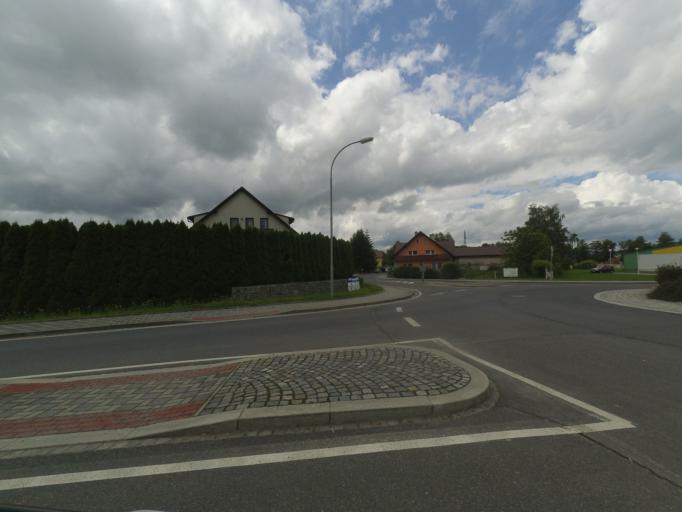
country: CZ
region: Plzensky
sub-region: Okres Klatovy
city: Nyrsko
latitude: 49.2958
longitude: 13.1505
